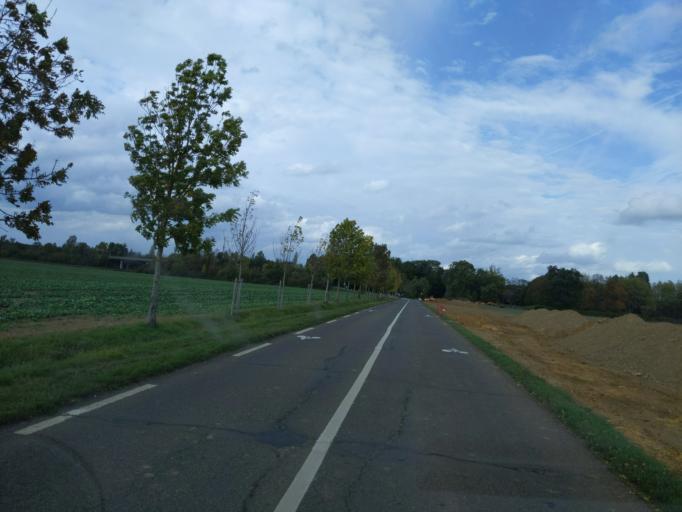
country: FR
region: Ile-de-France
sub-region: Departement des Yvelines
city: Rambouillet
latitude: 48.6527
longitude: 1.8466
